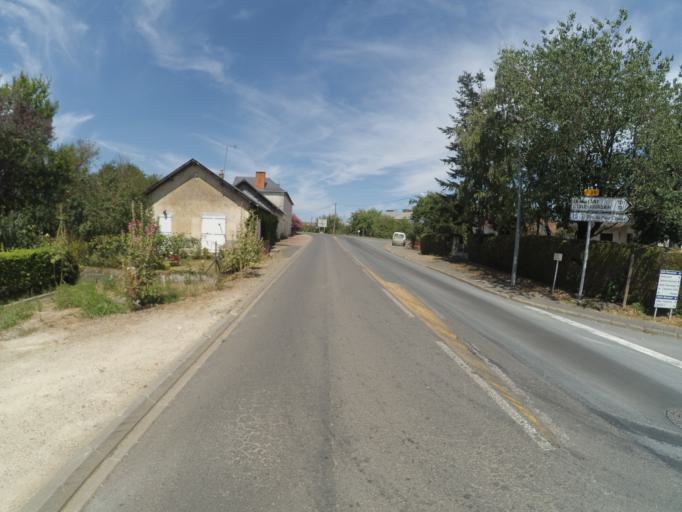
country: FR
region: Poitou-Charentes
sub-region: Departement de la Vienne
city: Usson-du-Poitou
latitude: 46.2198
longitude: 0.5303
